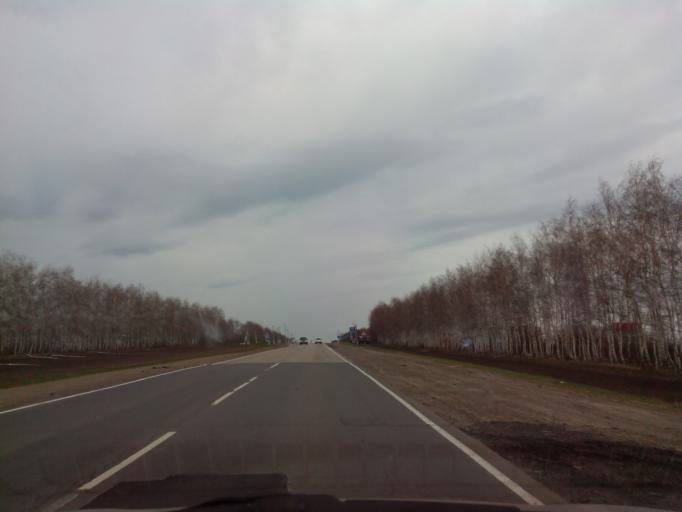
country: RU
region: Tambov
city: Znamenka
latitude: 52.4000
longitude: 41.3930
